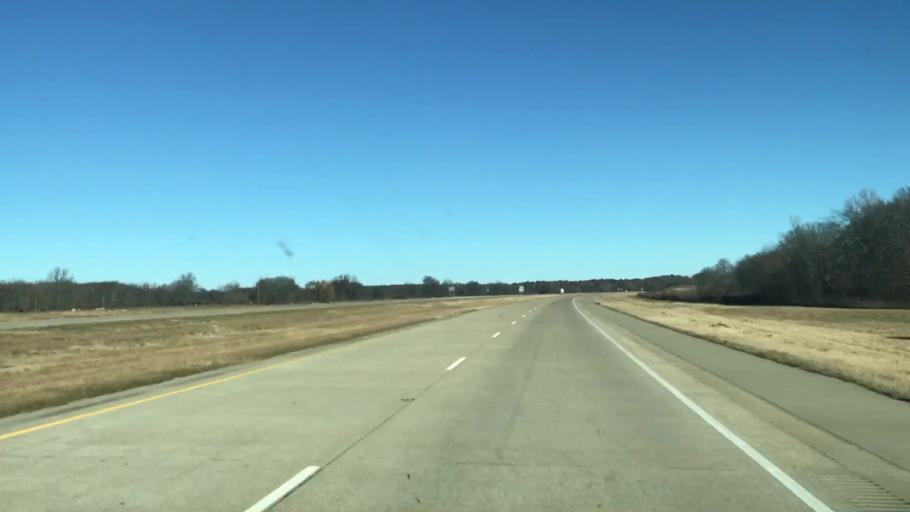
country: US
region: Louisiana
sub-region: Caddo Parish
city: Oil City
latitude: 32.7710
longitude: -93.8889
